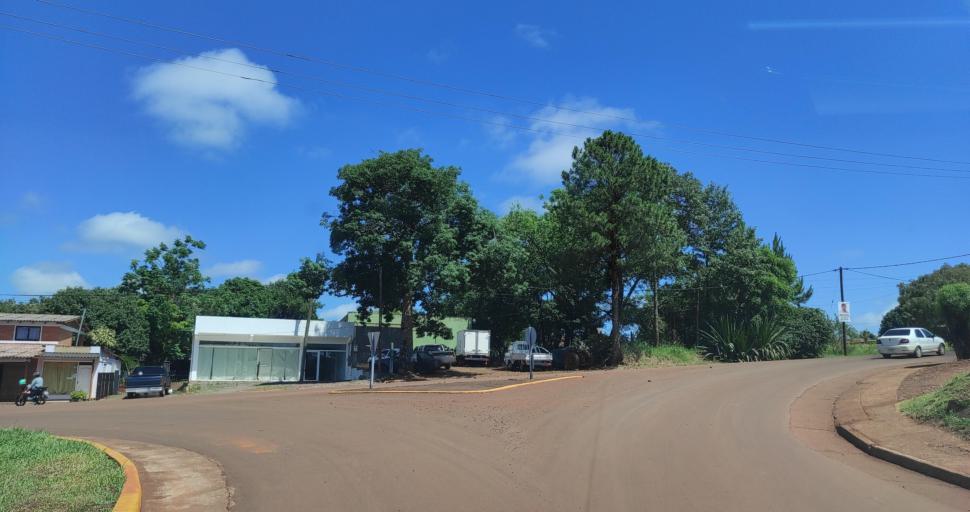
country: AR
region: Misiones
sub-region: Departamento de Veinticinco de Mayo
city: Veinticinco de Mayo
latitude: -27.3708
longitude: -54.7520
